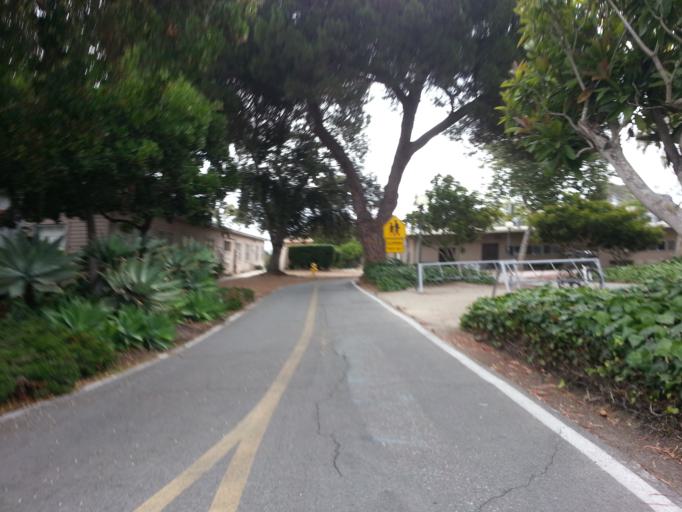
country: US
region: California
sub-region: Santa Barbara County
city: Isla Vista
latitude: 34.4167
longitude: -119.8441
